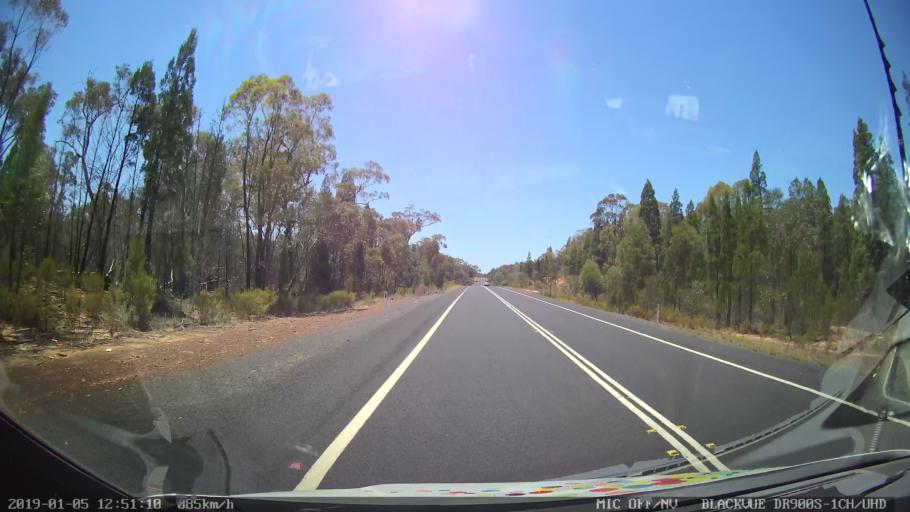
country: AU
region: New South Wales
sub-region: Warrumbungle Shire
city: Coonabarabran
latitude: -31.1205
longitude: 149.6350
